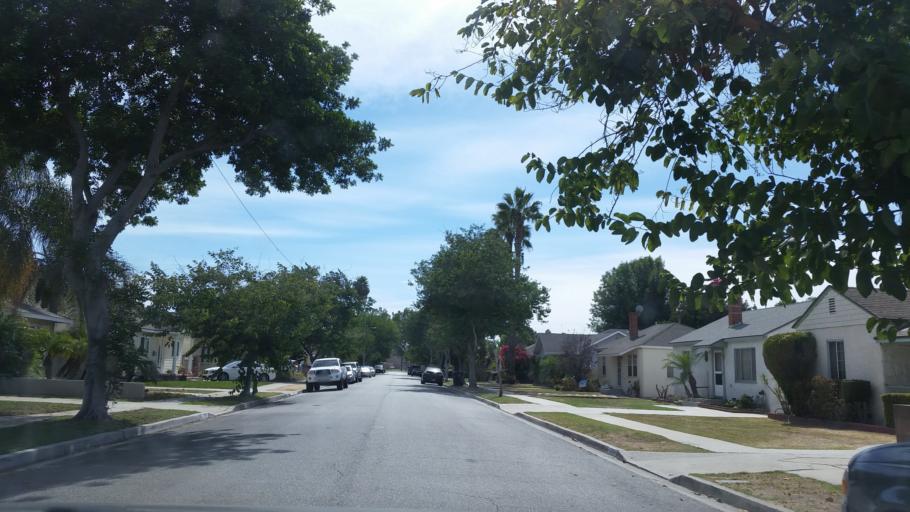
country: US
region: California
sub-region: Los Angeles County
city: Lakewood
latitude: 33.8627
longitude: -118.1309
